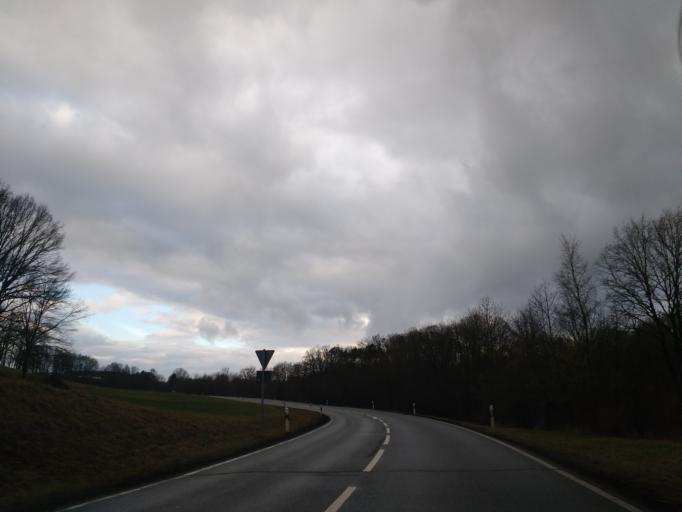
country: DE
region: Bavaria
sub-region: Regierungsbezirk Mittelfranken
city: Herzogenaurach
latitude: 49.5773
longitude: 10.8636
